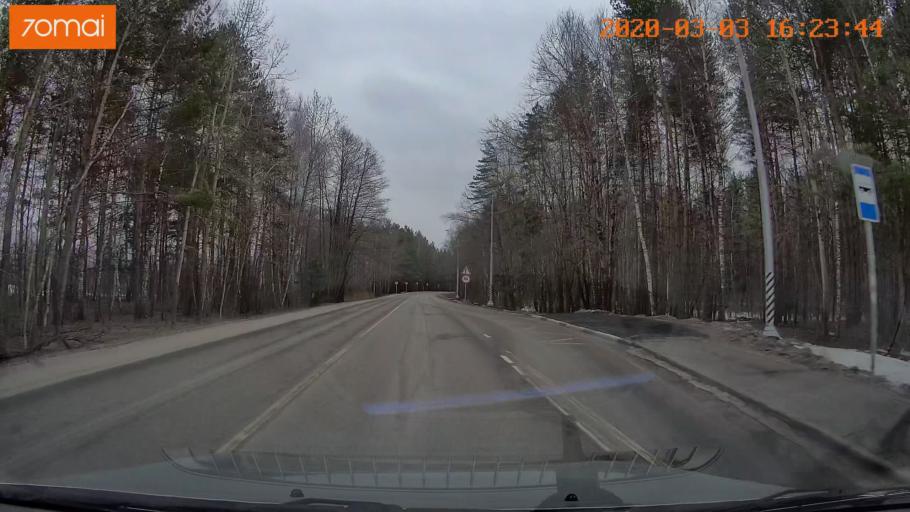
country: RU
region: Moskovskaya
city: Imeni Tsyurupy
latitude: 55.4769
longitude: 38.6563
